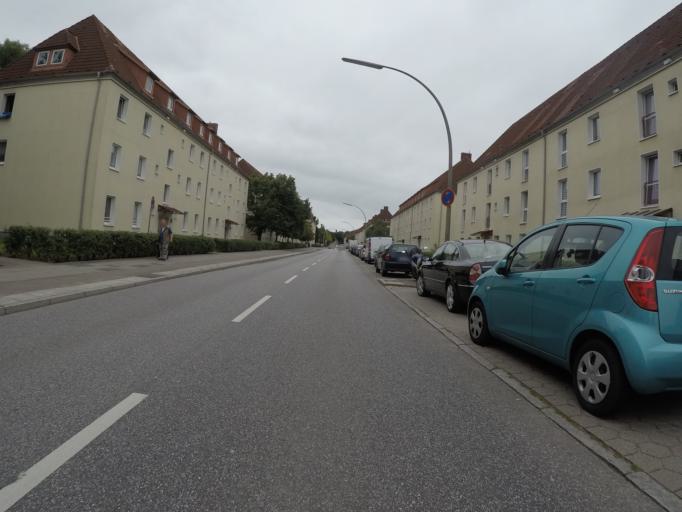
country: DE
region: Hamburg
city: Altona
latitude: 53.5314
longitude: 9.8789
